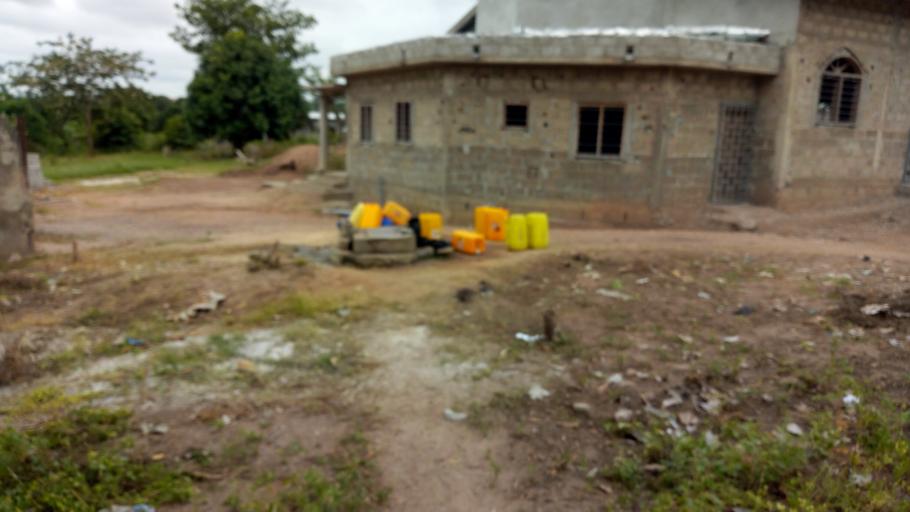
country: CI
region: Vallee du Bandama
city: Bouake
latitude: 7.6827
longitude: -5.0883
